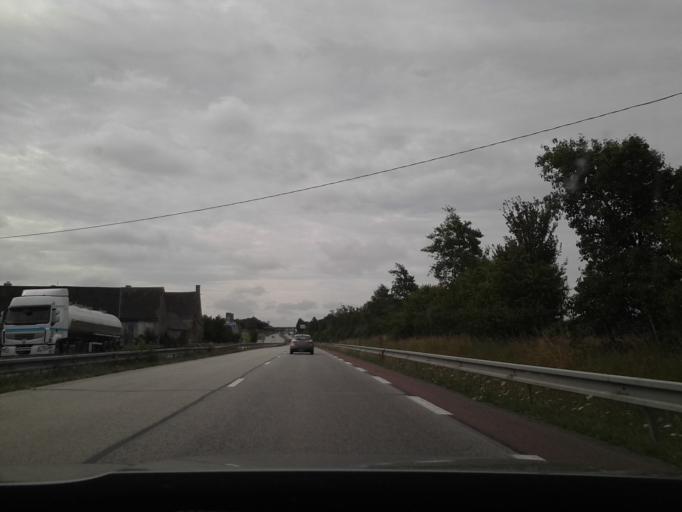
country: FR
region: Lower Normandy
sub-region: Departement de la Manche
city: Sainte-Mere-Eglise
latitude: 49.4301
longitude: -1.3343
